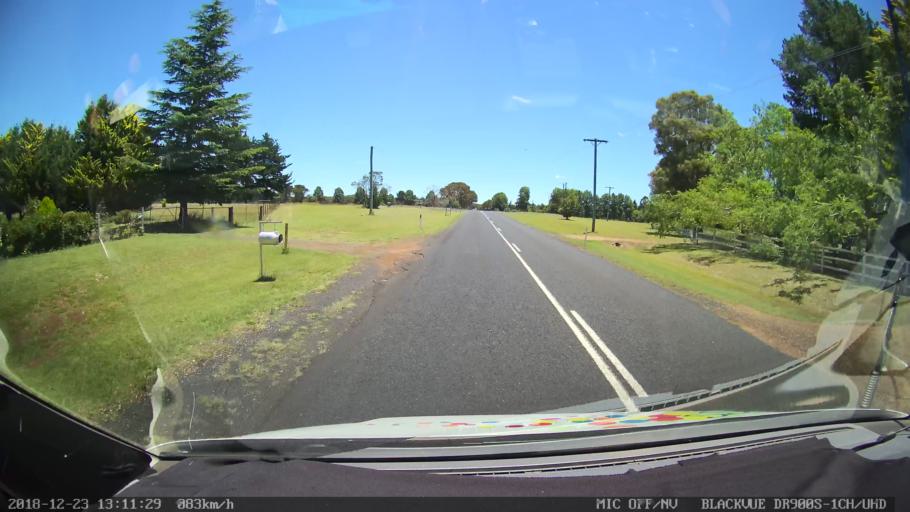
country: AU
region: New South Wales
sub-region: Armidale Dumaresq
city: Armidale
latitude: -30.5078
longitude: 151.5706
